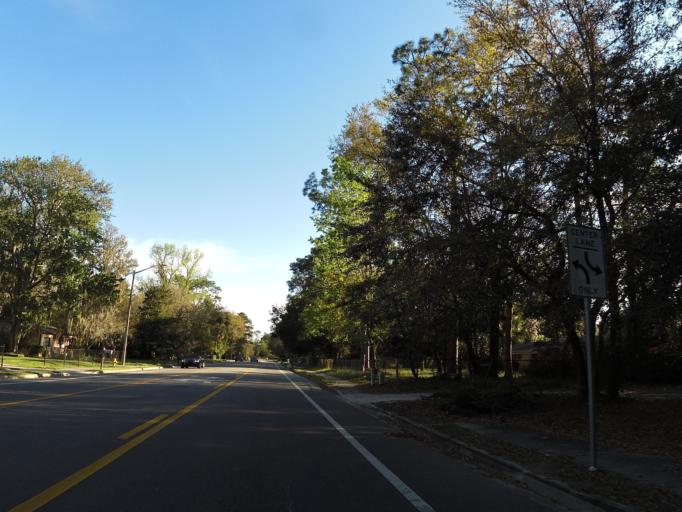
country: US
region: Florida
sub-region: Duval County
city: Jacksonville
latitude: 30.4668
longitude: -81.6178
